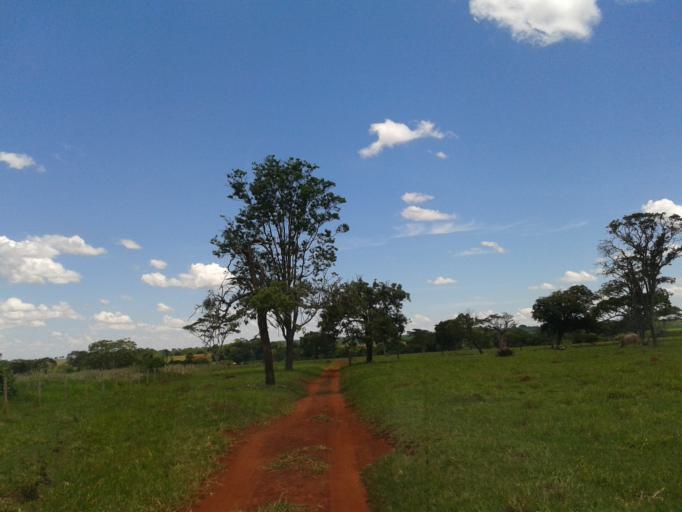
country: BR
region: Minas Gerais
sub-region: Centralina
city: Centralina
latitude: -18.7064
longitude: -49.1766
